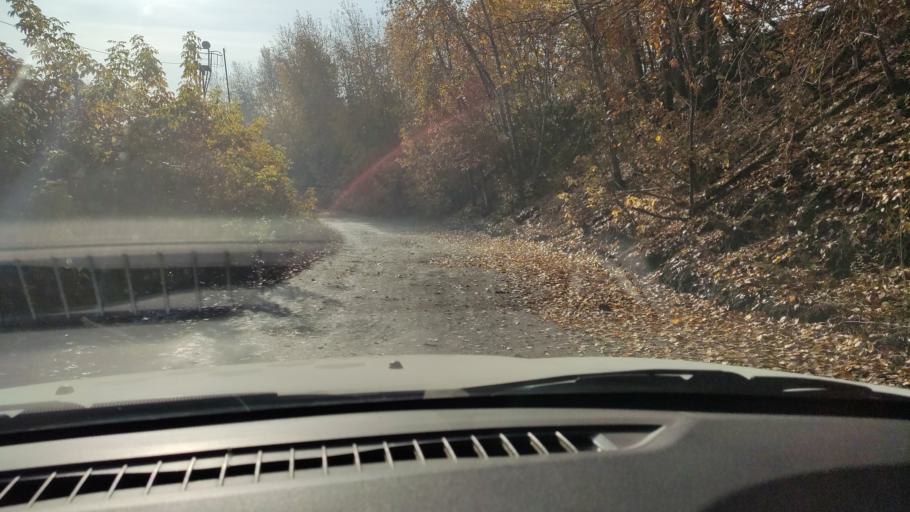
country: RU
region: Perm
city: Kondratovo
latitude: 58.0073
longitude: 56.1578
